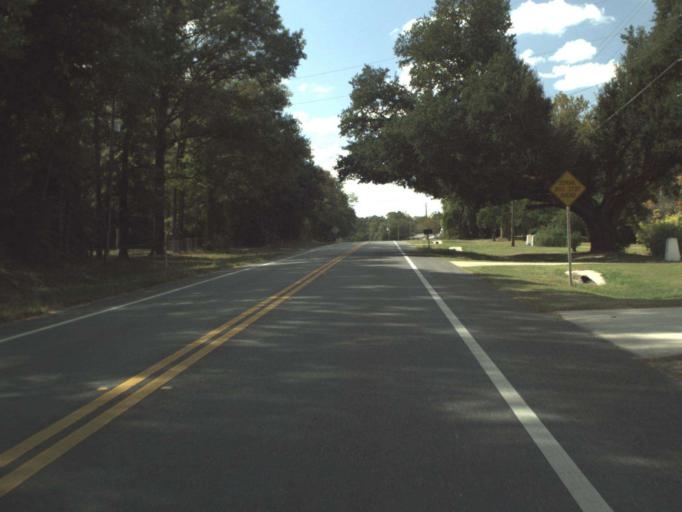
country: US
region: Florida
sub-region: Washington County
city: Chipley
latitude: 30.7632
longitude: -85.5720
